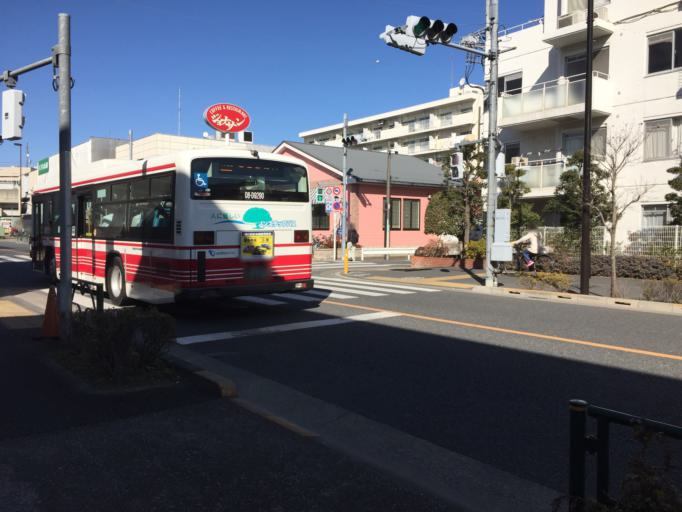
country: JP
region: Tokyo
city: Chofugaoka
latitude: 35.6327
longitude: 139.5802
